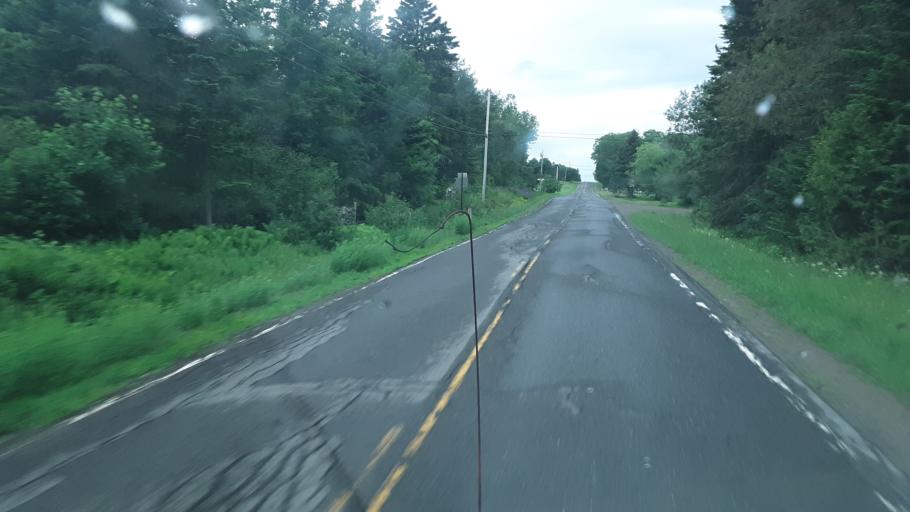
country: US
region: Maine
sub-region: Aroostook County
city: Caribou
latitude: 46.8791
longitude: -68.1913
